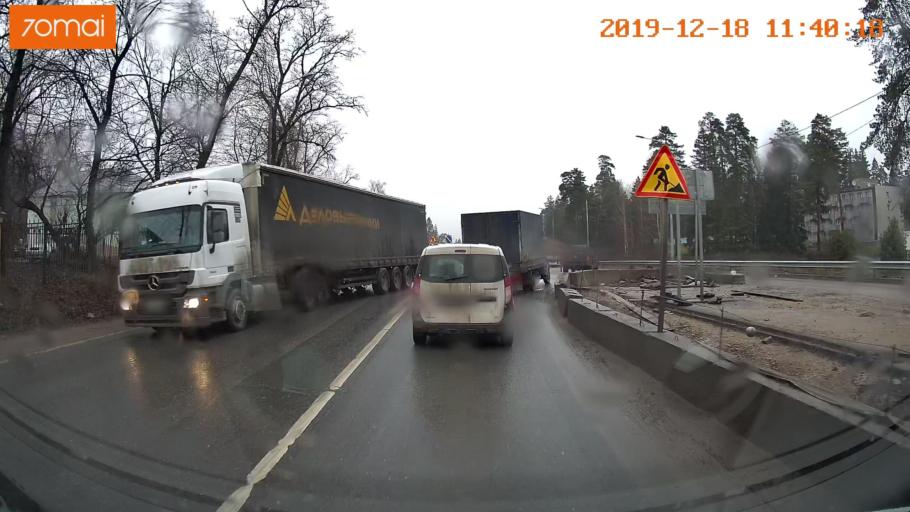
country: RU
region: Moskovskaya
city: Zvenigorod
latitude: 55.7056
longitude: 36.8771
